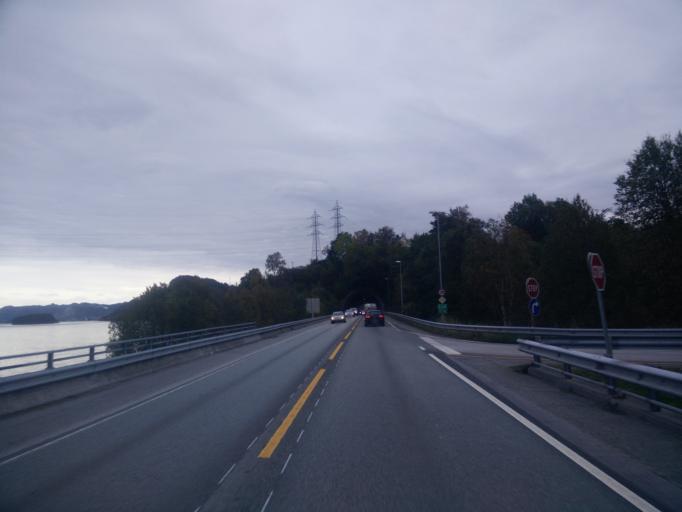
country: NO
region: More og Romsdal
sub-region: Sula
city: Langevag
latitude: 62.4702
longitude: 6.2435
